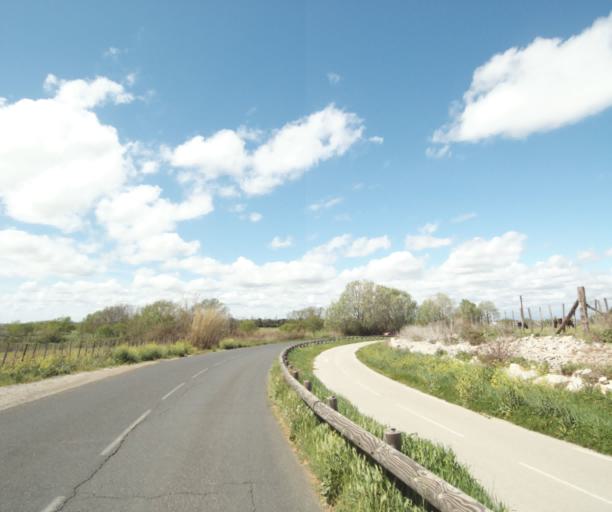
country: FR
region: Languedoc-Roussillon
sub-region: Departement de l'Herault
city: Lattes
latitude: 43.5602
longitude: 3.9235
